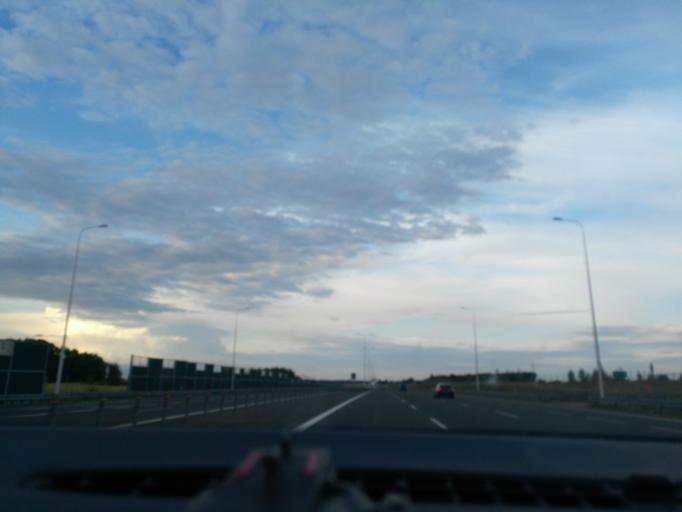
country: PL
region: Lublin Voivodeship
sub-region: Powiat lubelski
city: Jastkow
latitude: 51.2889
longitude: 22.4615
